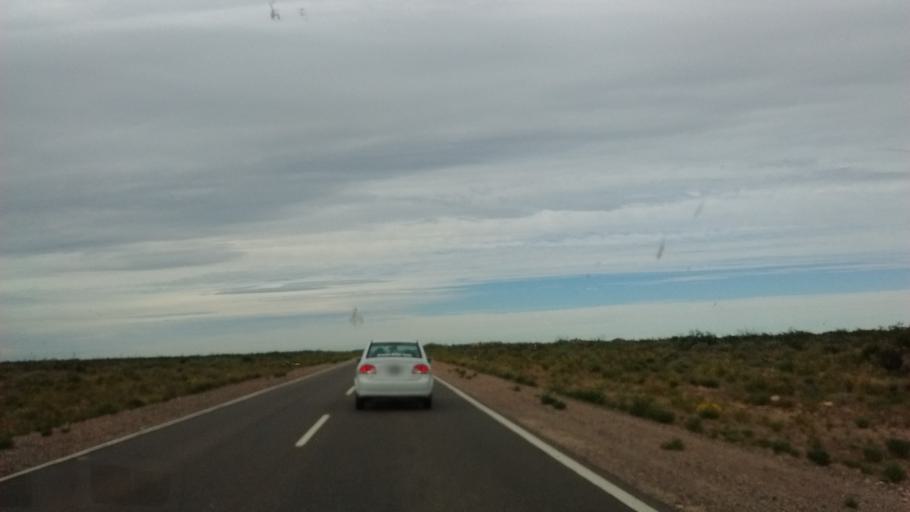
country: AR
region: Rio Negro
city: Contraalmirante Cordero
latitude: -38.3441
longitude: -68.0124
